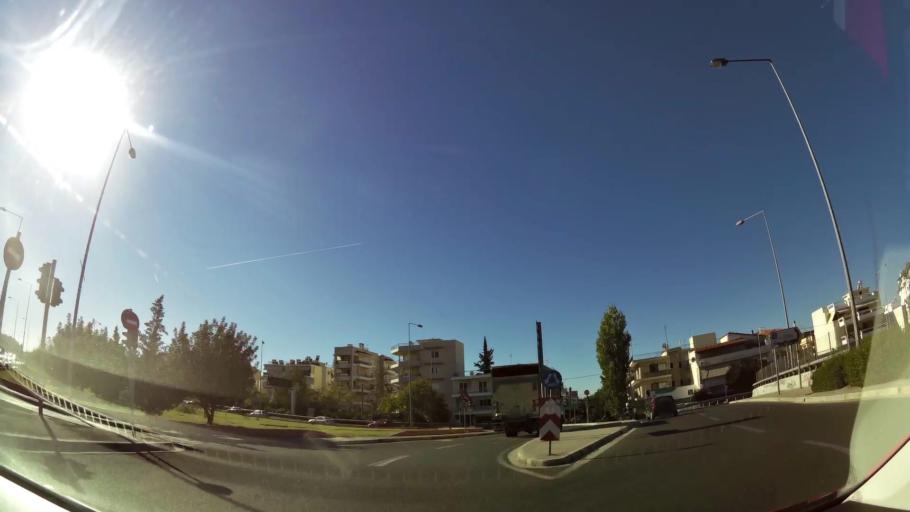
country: GR
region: Attica
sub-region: Nomarchia Athinas
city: Agia Paraskevi
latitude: 38.0211
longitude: 23.8364
